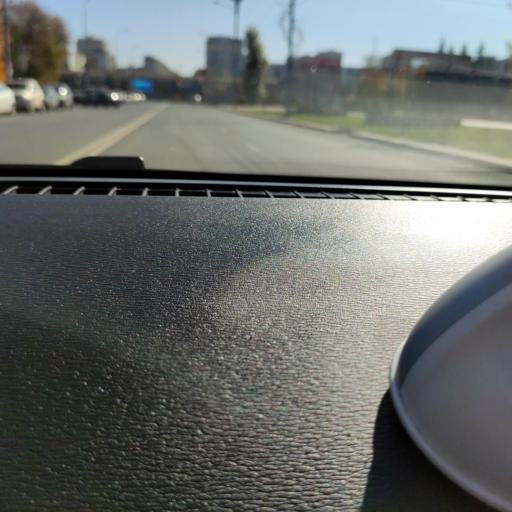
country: RU
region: Samara
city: Samara
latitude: 53.2051
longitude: 50.1390
